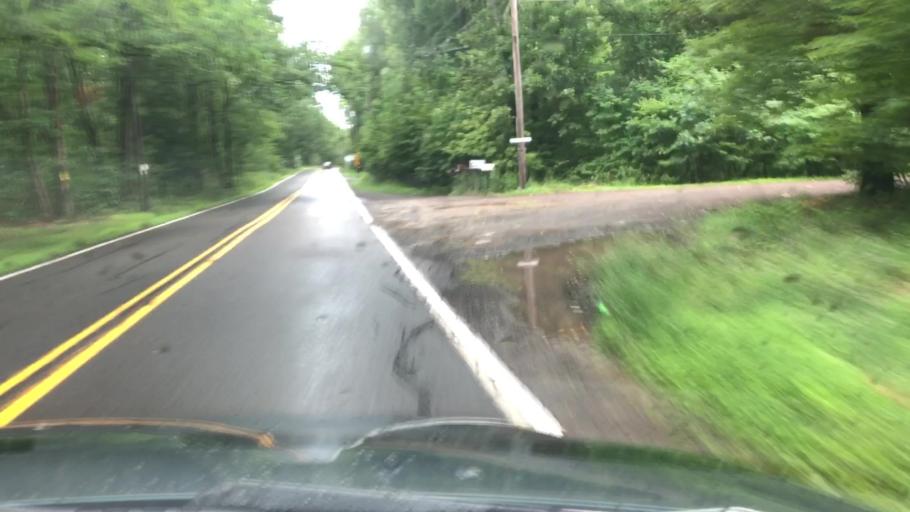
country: US
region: Pennsylvania
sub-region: Monroe County
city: Mountainhome
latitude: 41.2641
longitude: -75.2377
